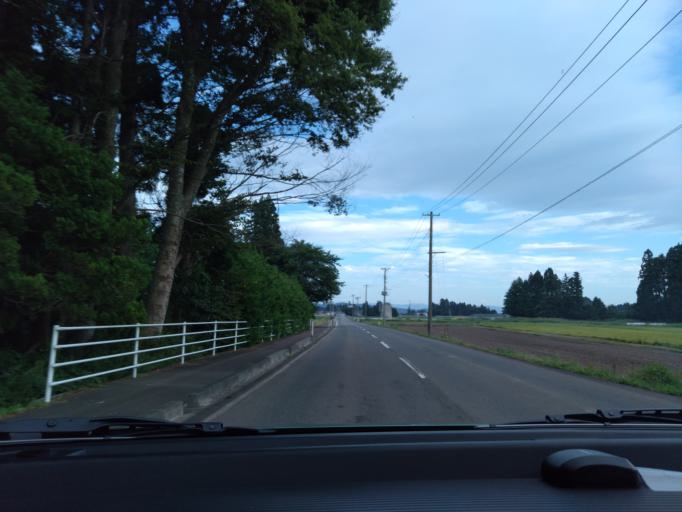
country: JP
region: Iwate
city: Kitakami
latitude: 39.3273
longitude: 141.0592
